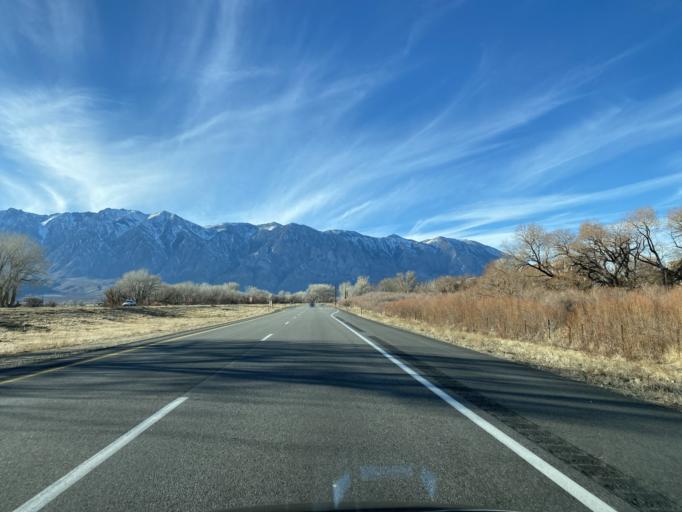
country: US
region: California
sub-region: Inyo County
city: West Bishop
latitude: 37.4051
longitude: -118.5407
